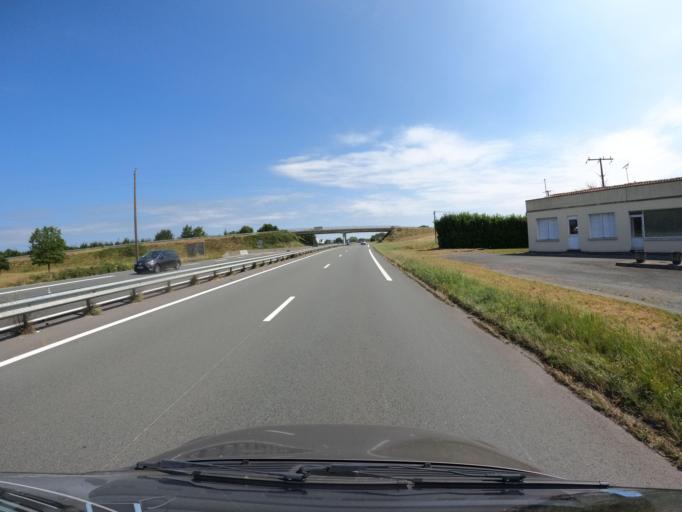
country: FR
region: Poitou-Charentes
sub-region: Departement des Deux-Sevres
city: Mauze-sur-le-Mignon
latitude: 46.1994
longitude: -0.6572
